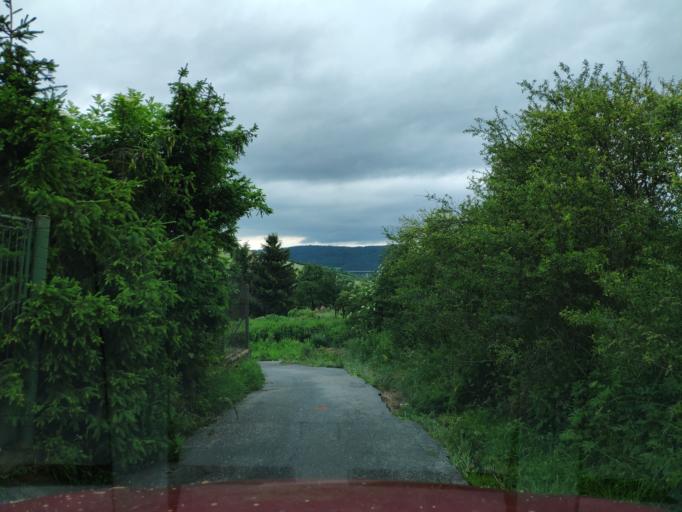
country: SK
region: Presovsky
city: Sabinov
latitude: 49.0415
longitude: 21.0166
